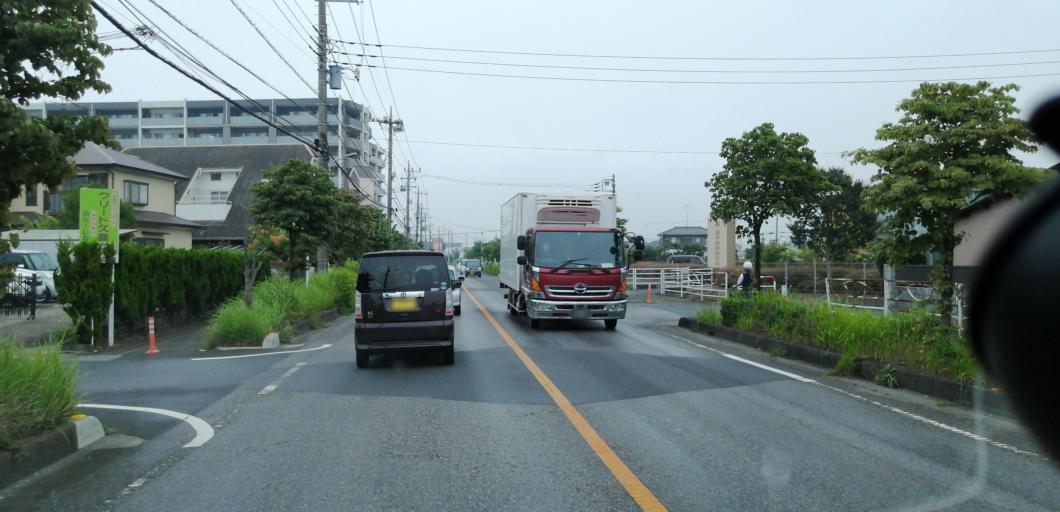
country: JP
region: Saitama
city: Kukichuo
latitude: 36.0943
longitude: 139.6851
